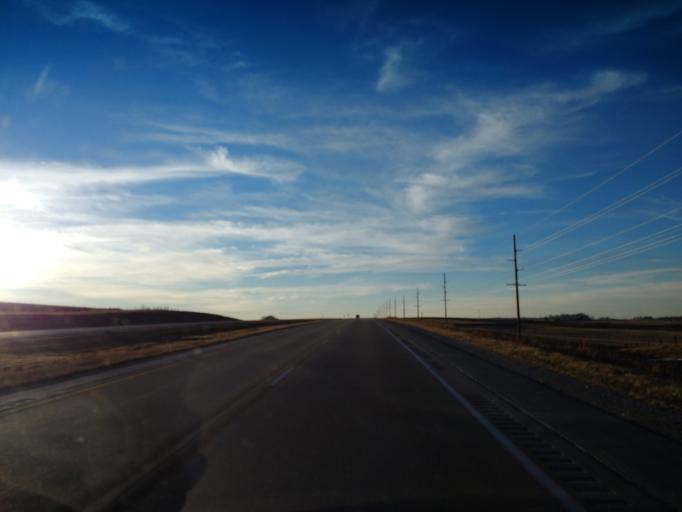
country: US
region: Iowa
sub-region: Ida County
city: Holstein
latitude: 42.4751
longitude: -95.4799
